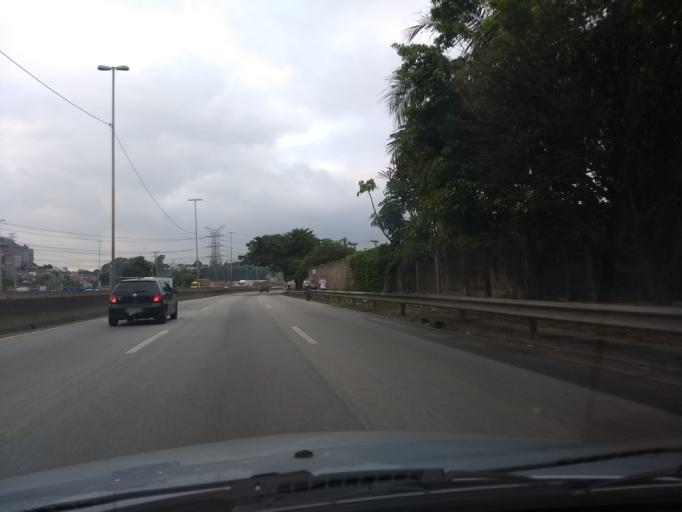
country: BR
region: Sao Paulo
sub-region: Guarulhos
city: Guarulhos
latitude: -23.4722
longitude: -46.5641
